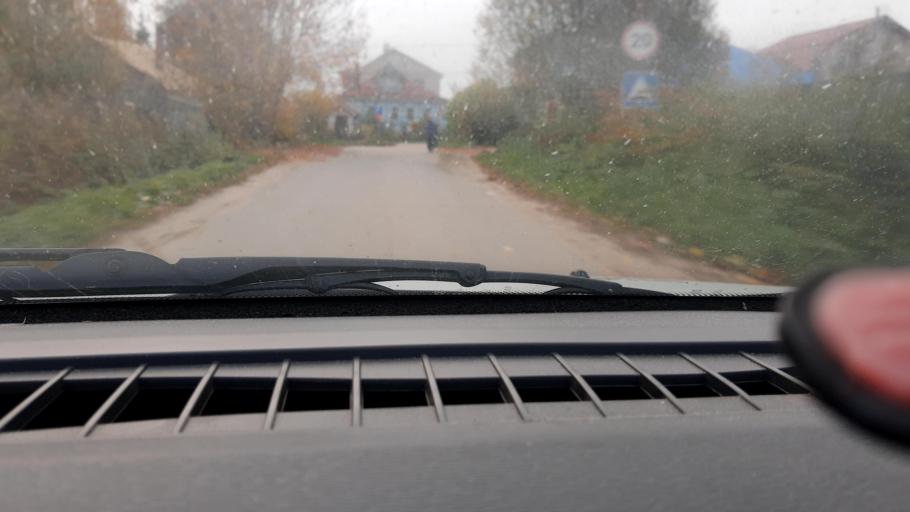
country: RU
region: Nizjnij Novgorod
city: Afonino
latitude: 56.2672
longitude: 44.0522
